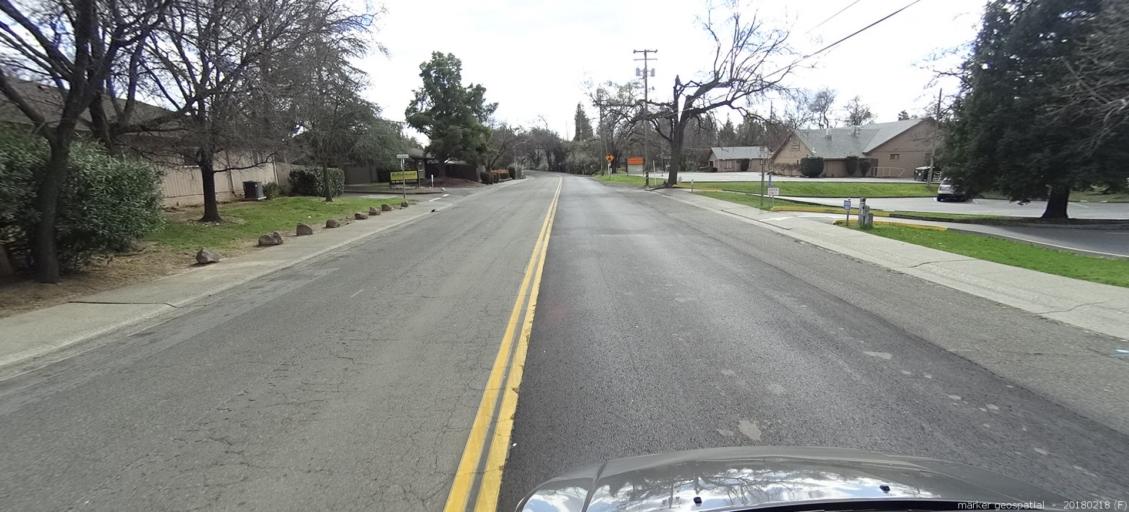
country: US
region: California
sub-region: Sacramento County
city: Orangevale
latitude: 38.6723
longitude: -121.2071
